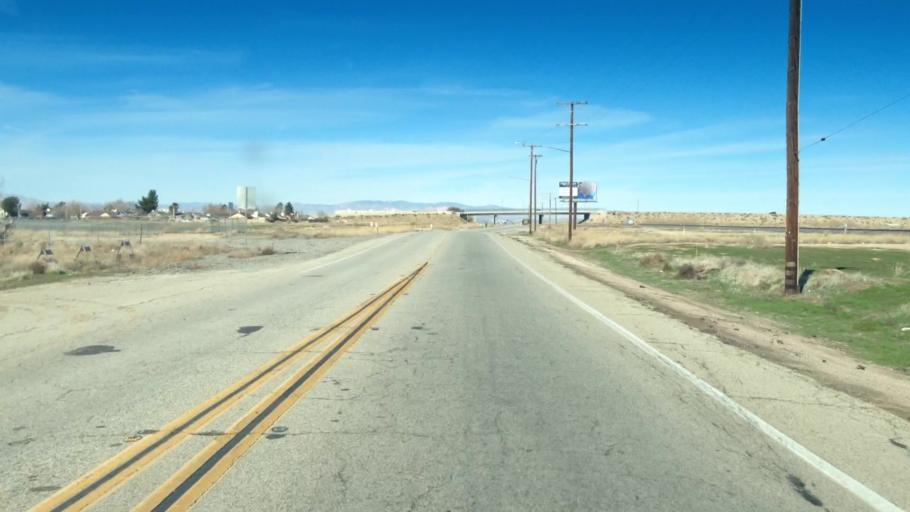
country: US
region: California
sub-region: Los Angeles County
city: Lancaster
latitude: 34.7128
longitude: -118.1392
